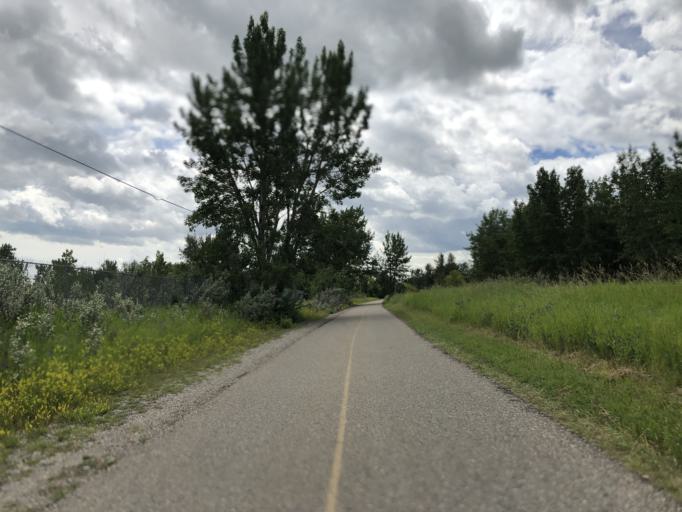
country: CA
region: Alberta
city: Calgary
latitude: 51.0254
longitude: -114.0114
